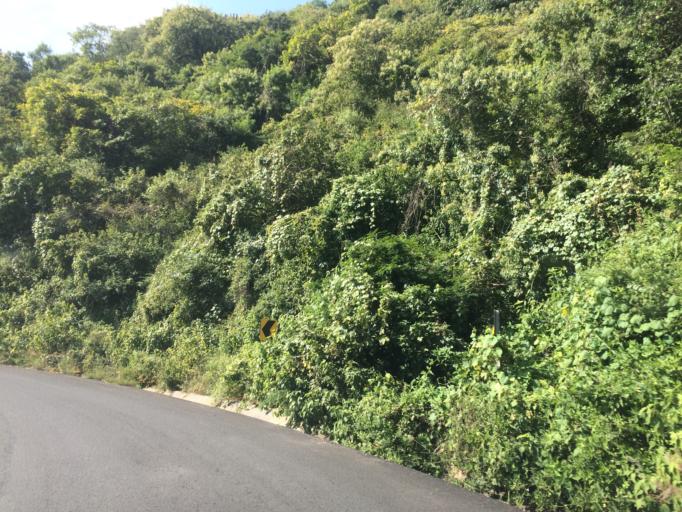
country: MX
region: Nayarit
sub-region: Ahuacatlan
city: Ahuacatlan
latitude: 21.0268
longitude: -104.4761
